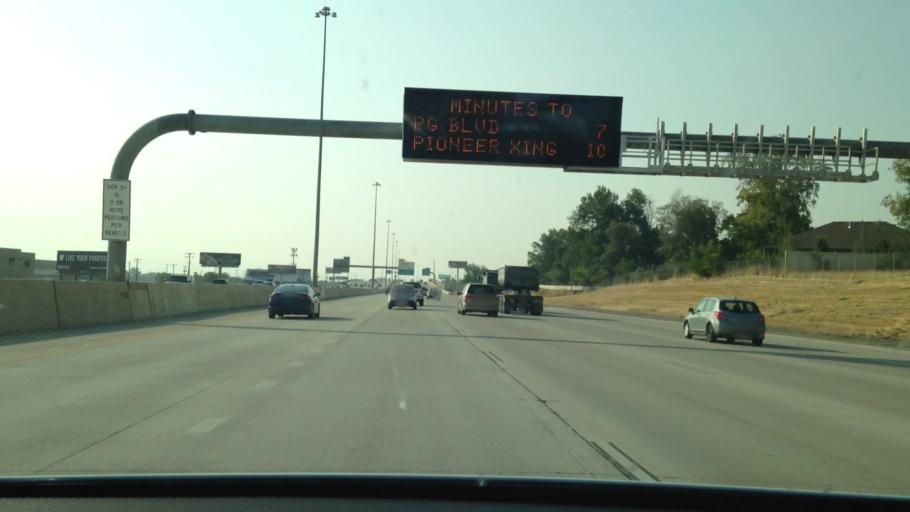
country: US
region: Utah
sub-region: Utah County
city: Orem
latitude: 40.2552
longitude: -111.6992
